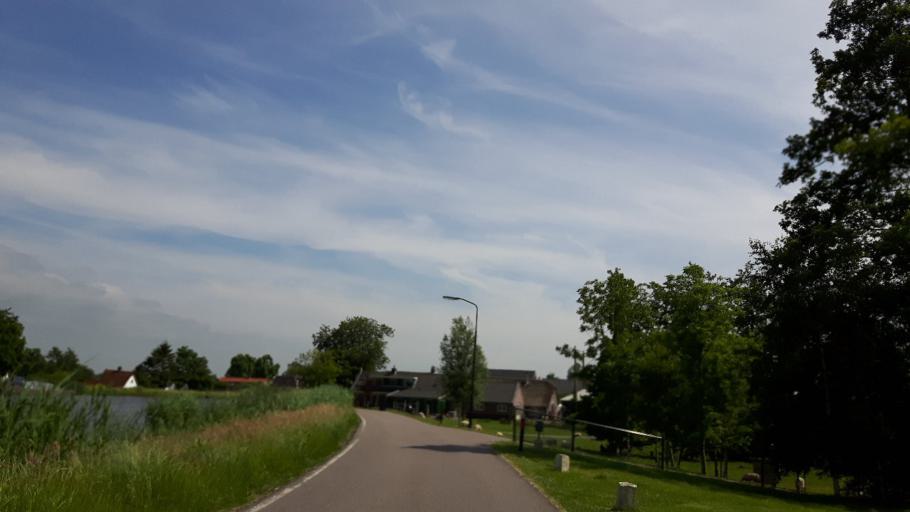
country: NL
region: North Holland
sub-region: Gemeente Uithoorn
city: Uithoorn
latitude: 52.2081
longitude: 4.8135
